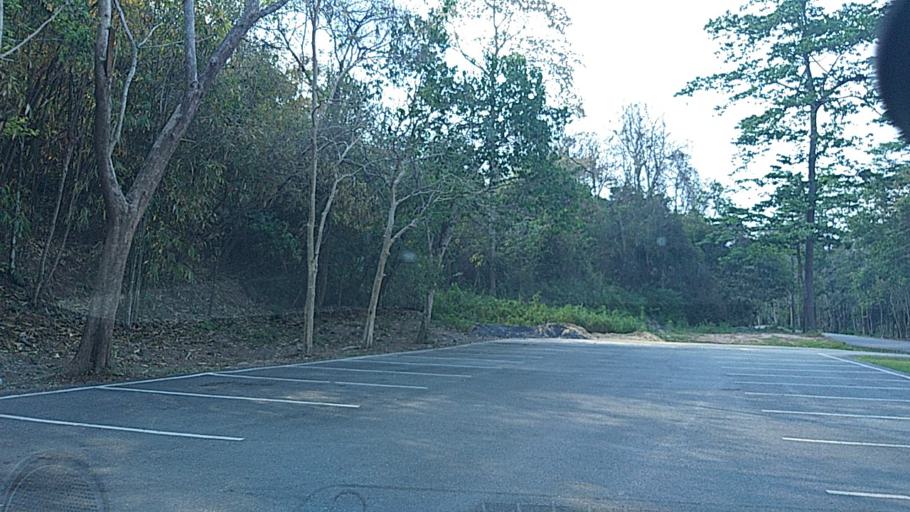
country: TH
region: Sara Buri
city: Wihan Daeng
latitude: 14.4383
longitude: 100.9616
